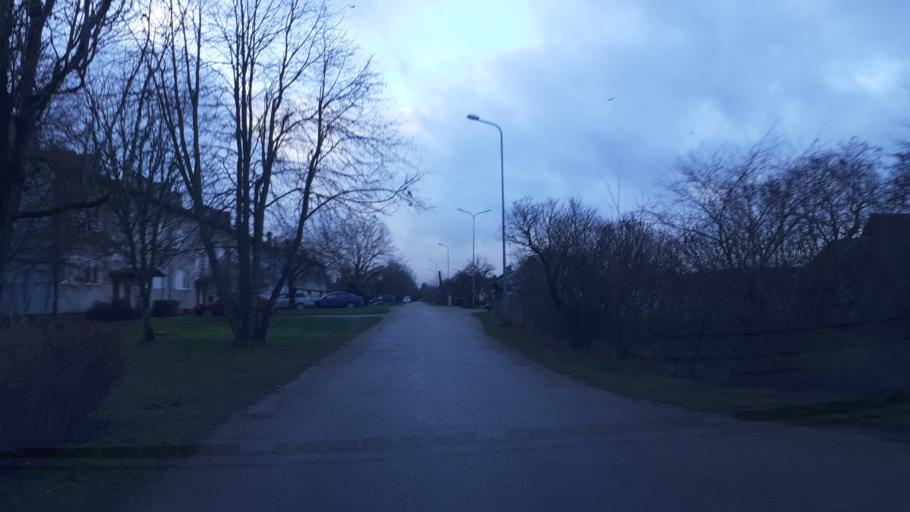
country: LV
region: Talsu Rajons
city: Stende
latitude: 57.0668
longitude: 22.2887
